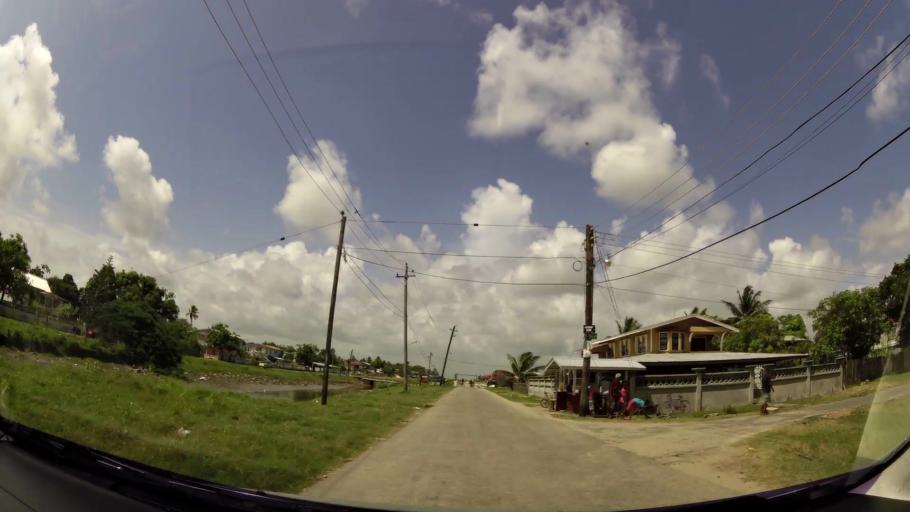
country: GY
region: Demerara-Mahaica
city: Mahaica Village
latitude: 6.7692
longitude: -58.0112
